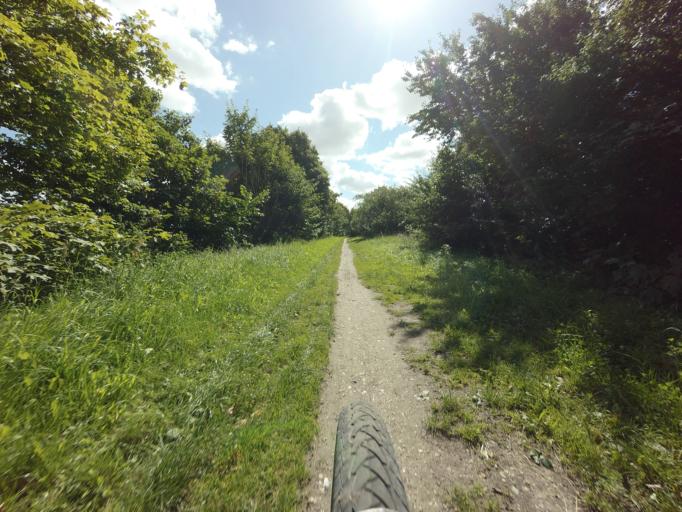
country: DK
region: Central Jutland
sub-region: Horsens Kommune
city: Horsens
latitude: 55.8928
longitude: 9.7750
